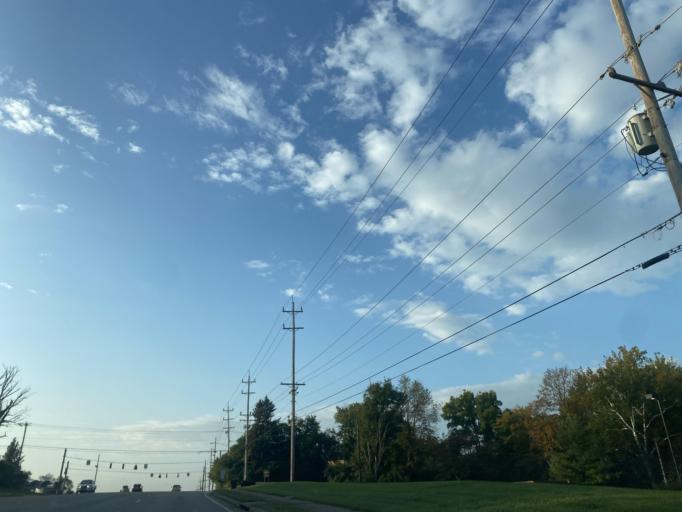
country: US
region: Kentucky
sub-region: Campbell County
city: Alexandria
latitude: 38.9592
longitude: -84.3931
